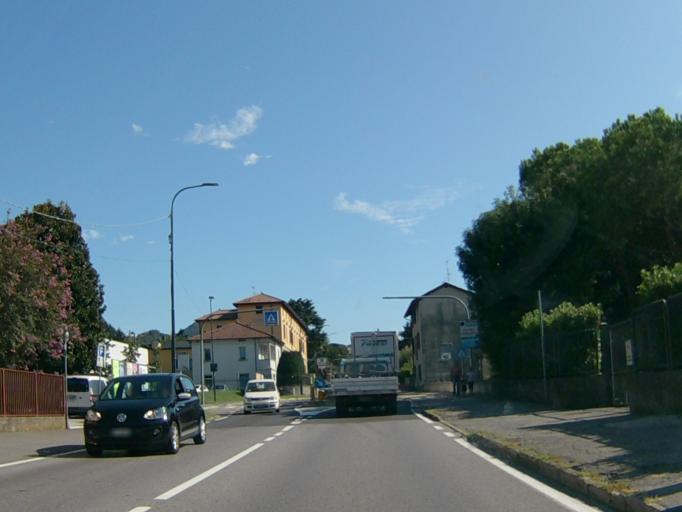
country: IT
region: Lombardy
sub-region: Provincia di Lecco
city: Calolziocorte
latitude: 45.7975
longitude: 9.4342
